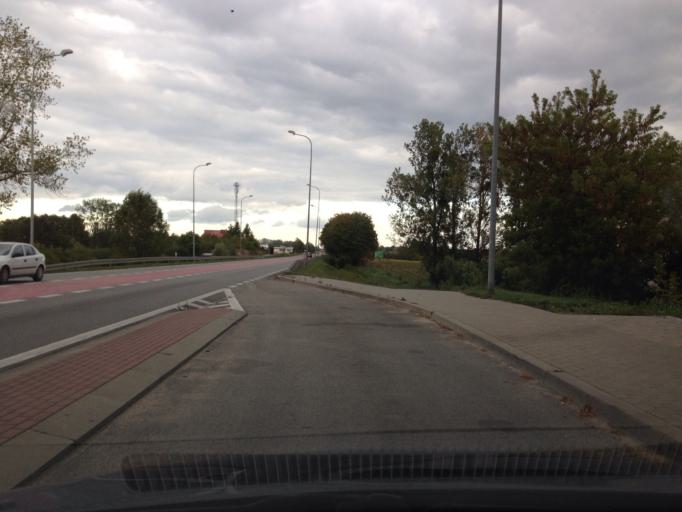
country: PL
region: Kujawsko-Pomorskie
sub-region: Powiat lipnowski
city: Lipno
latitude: 52.8524
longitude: 19.1802
